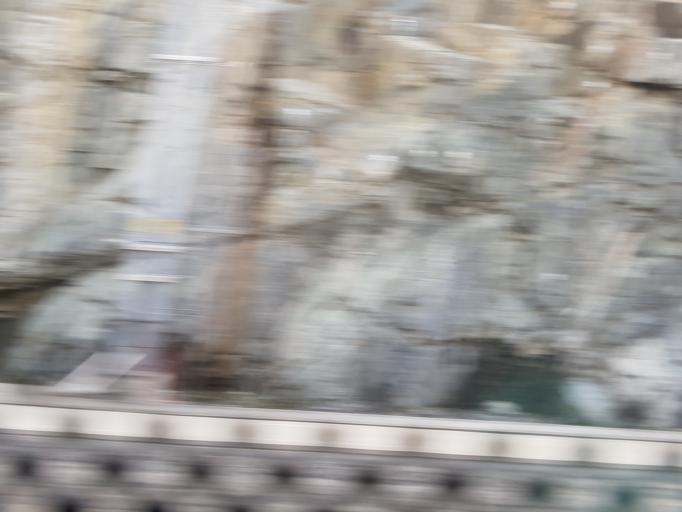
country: NO
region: Akershus
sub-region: Eidsvoll
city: Eidsvoll
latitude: 60.4343
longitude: 11.2396
